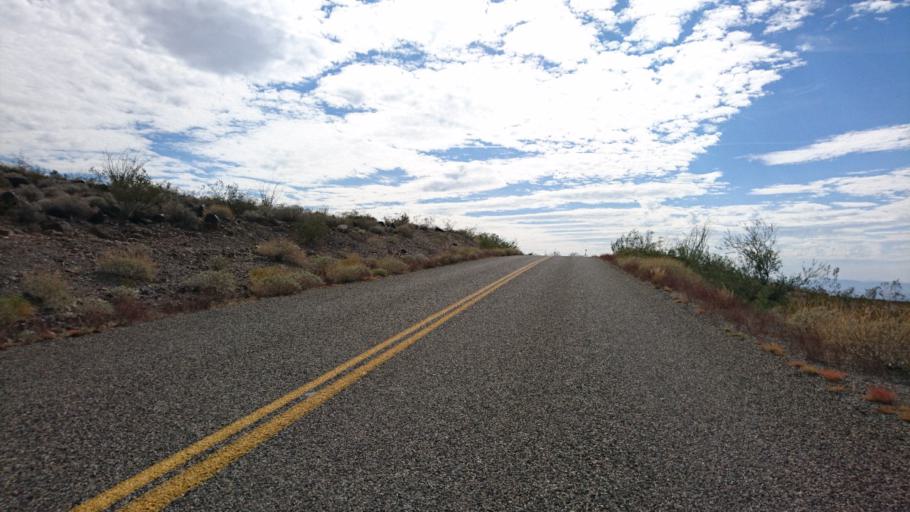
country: US
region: Arizona
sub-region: Mohave County
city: Mohave Valley
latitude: 34.9595
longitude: -114.4094
